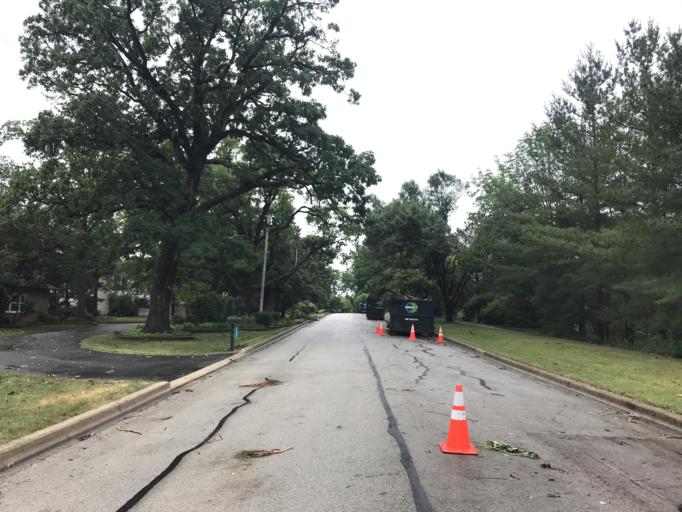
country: US
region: Illinois
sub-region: DuPage County
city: Woodridge
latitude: 41.7453
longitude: -88.0887
